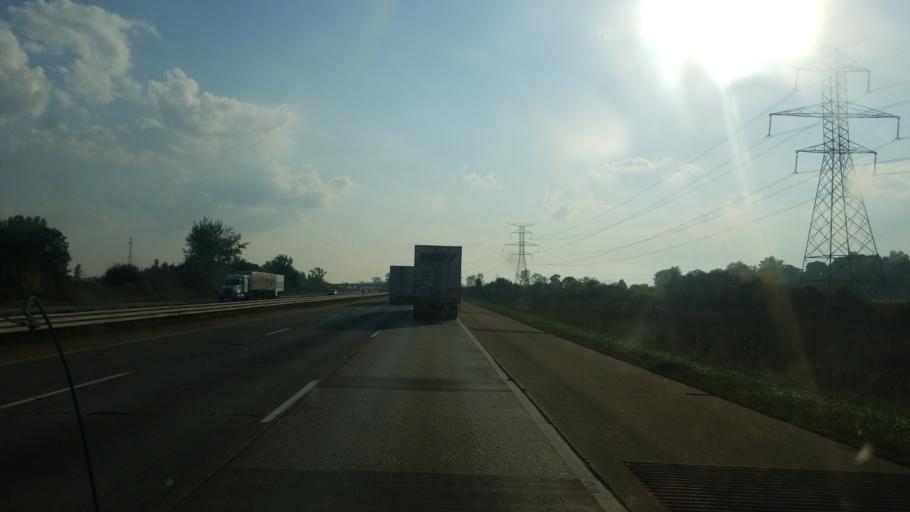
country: US
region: Michigan
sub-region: Monroe County
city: Luna Pier
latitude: 41.8158
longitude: -83.4446
